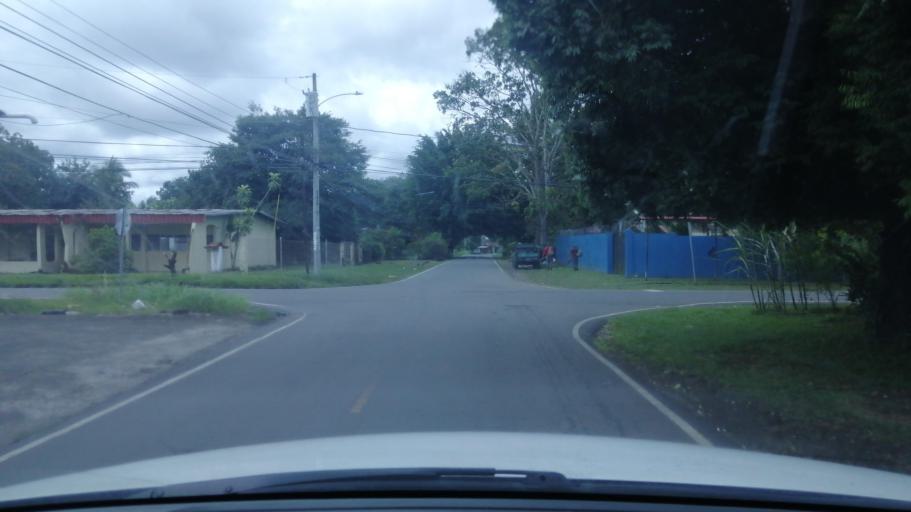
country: PA
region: Chiriqui
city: David
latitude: 8.4195
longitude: -82.4284
